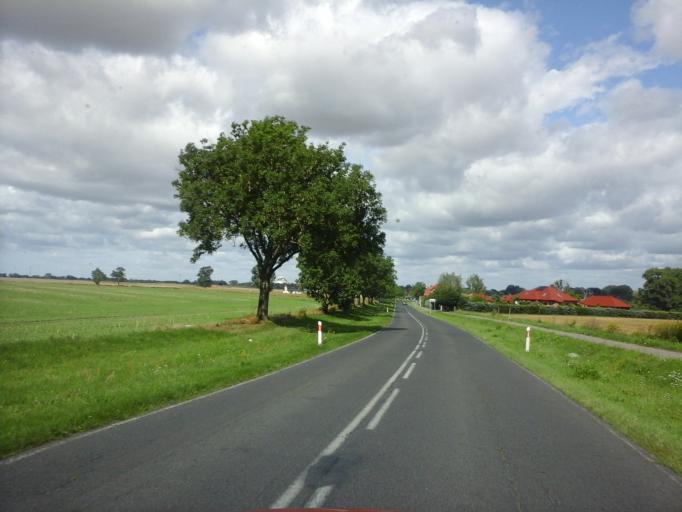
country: PL
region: West Pomeranian Voivodeship
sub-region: Powiat stargardzki
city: Stargard Szczecinski
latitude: 53.2922
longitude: 15.0612
